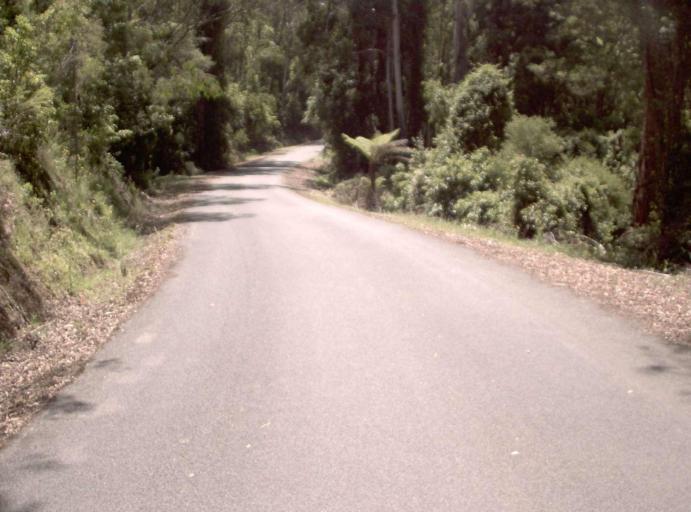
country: AU
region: New South Wales
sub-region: Bombala
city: Bombala
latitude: -37.4947
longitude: 148.9255
